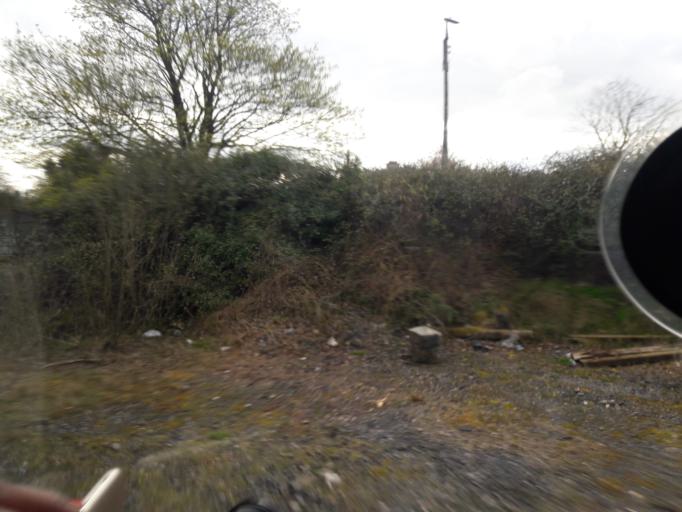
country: IE
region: Leinster
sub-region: An Iarmhi
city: An Muileann gCearr
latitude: 53.5280
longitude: -7.3475
